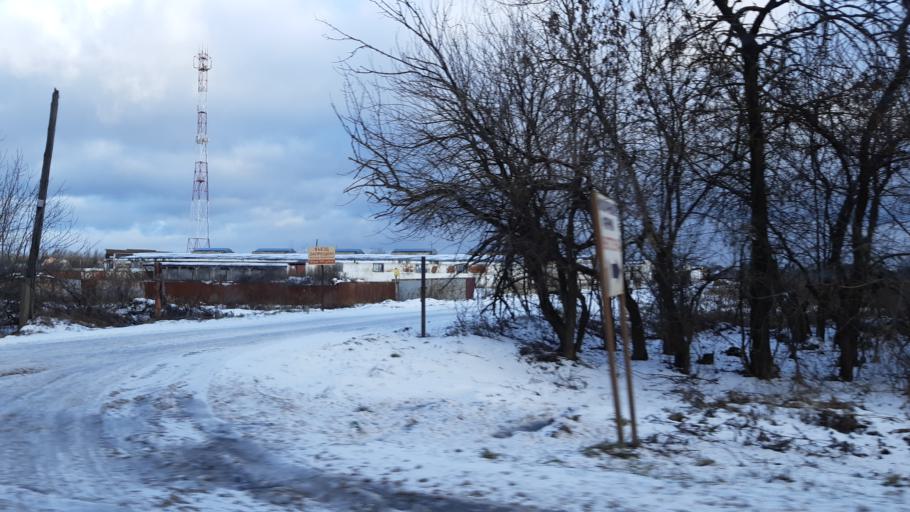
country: RU
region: Moskovskaya
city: Noginsk-9
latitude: 56.0189
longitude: 38.5572
